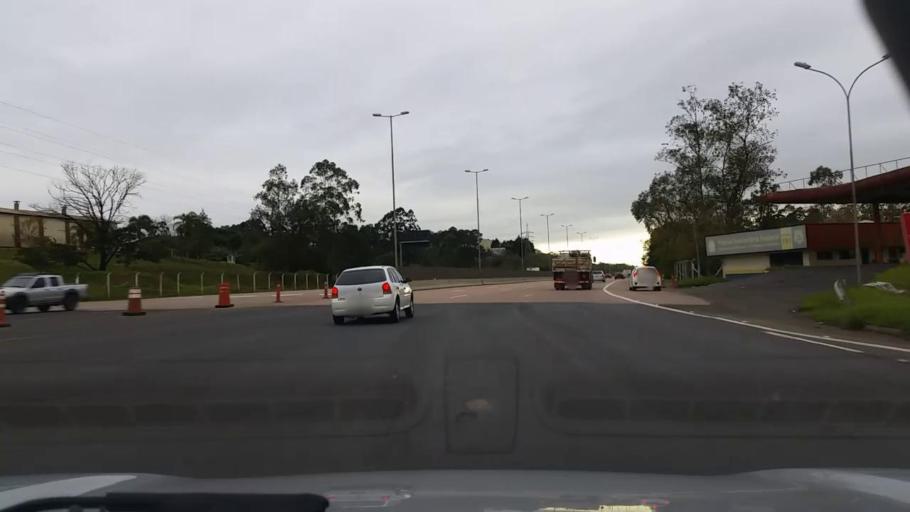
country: BR
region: Rio Grande do Sul
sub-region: Gravatai
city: Gravatai
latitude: -29.9552
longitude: -51.0291
